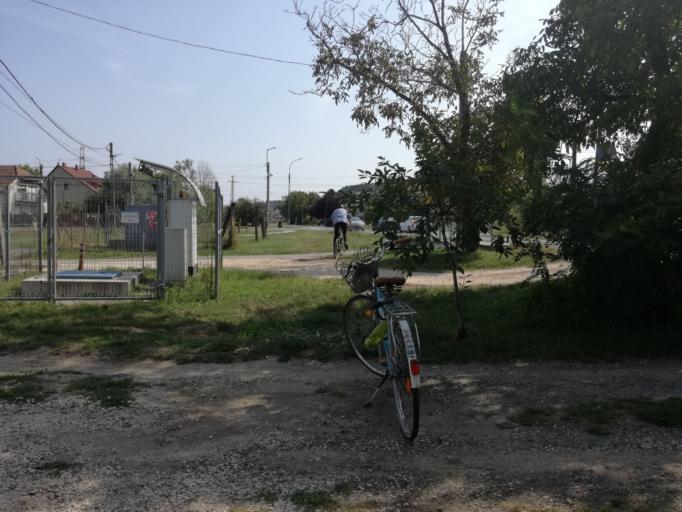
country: HU
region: Pest
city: Erd
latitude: 47.3655
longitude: 18.9272
